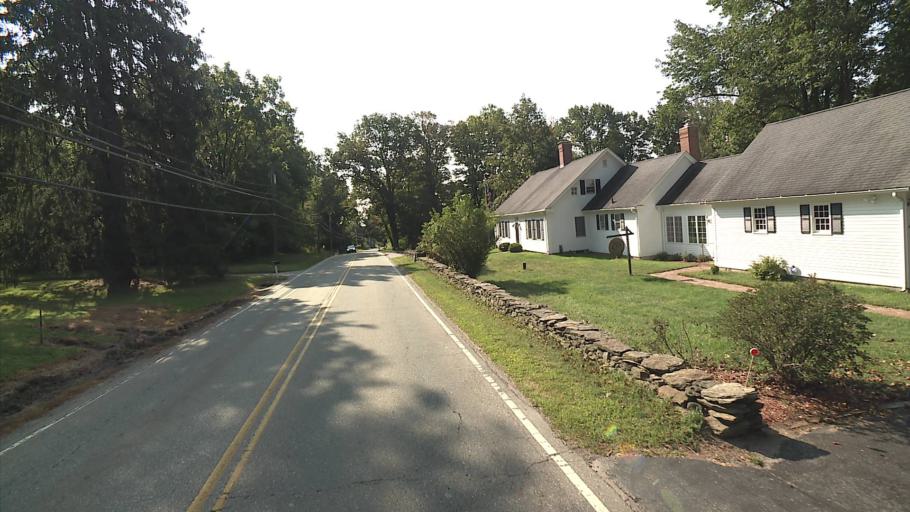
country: US
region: Connecticut
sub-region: Windham County
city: South Windham
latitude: 41.5989
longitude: -72.1658
